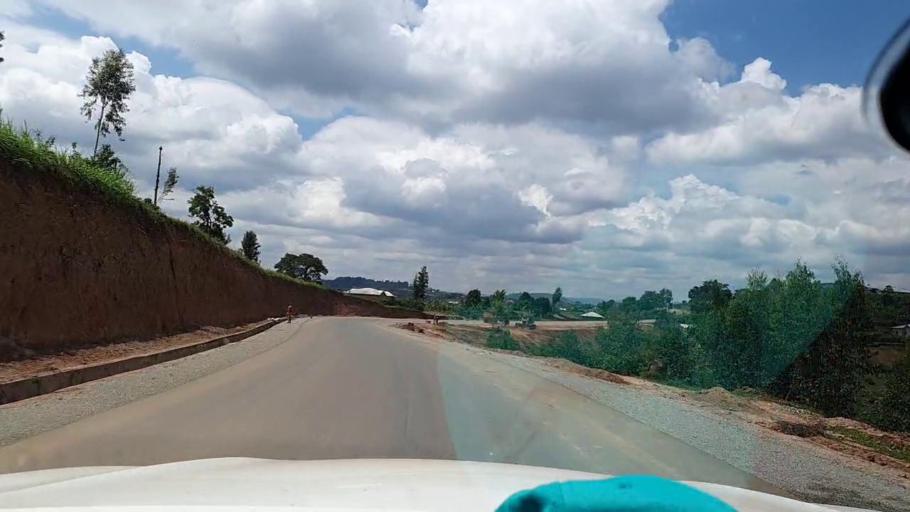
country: RW
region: Southern Province
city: Nzega
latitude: -2.6444
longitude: 29.5723
